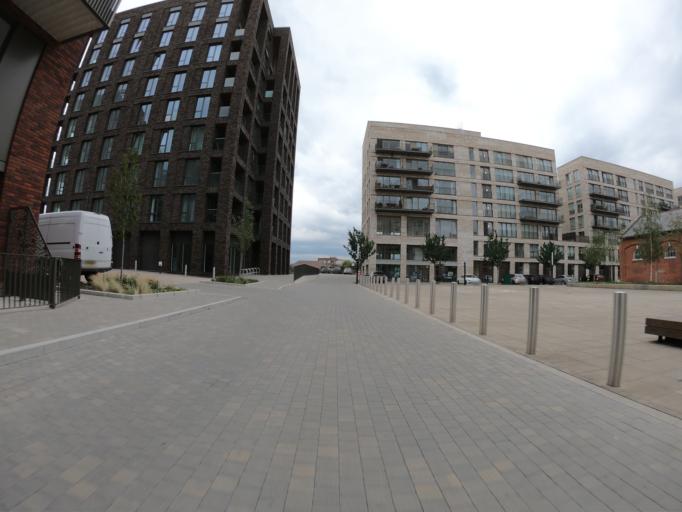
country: GB
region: England
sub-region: Greater London
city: Woolwich
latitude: 51.5059
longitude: 0.0770
